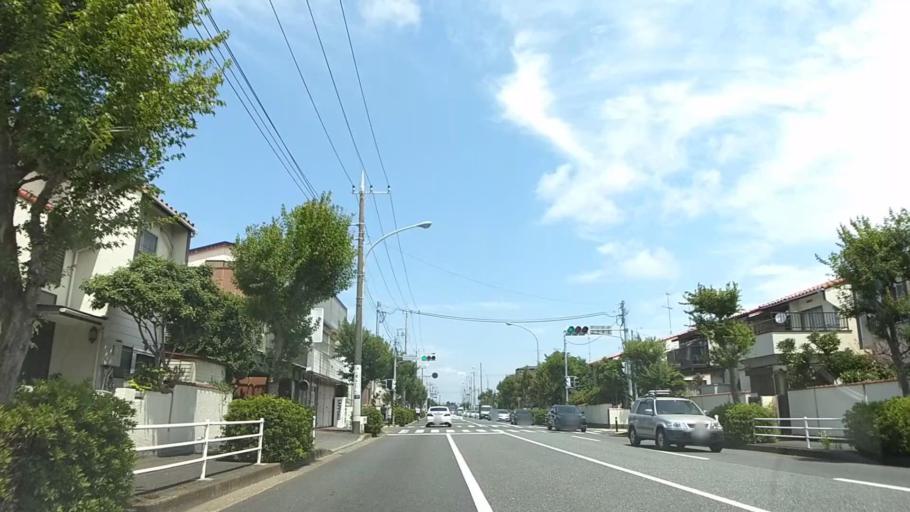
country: JP
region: Kanagawa
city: Minami-rinkan
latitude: 35.4448
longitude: 139.4843
